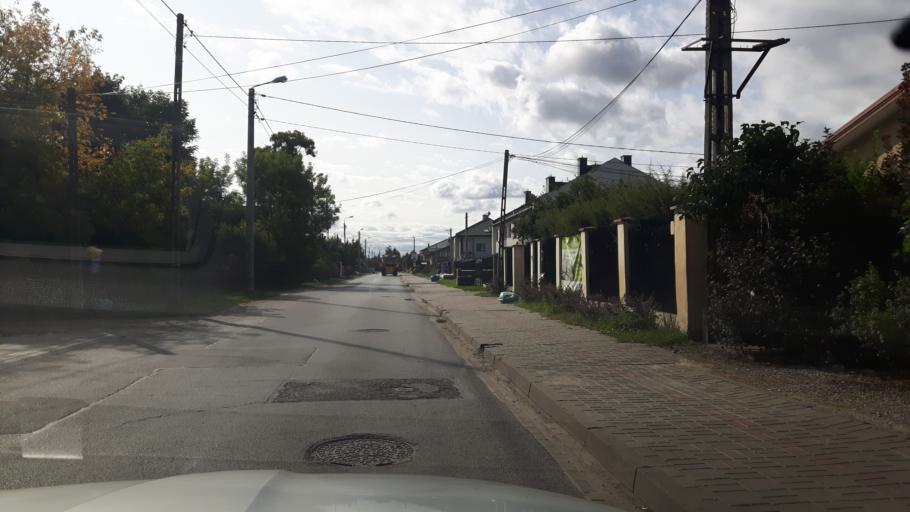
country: PL
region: Masovian Voivodeship
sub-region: Powiat wolominski
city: Marki
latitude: 52.3316
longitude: 21.0920
